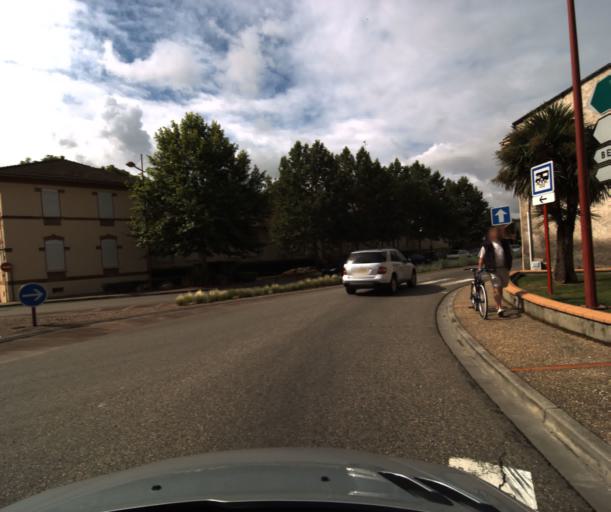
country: FR
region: Midi-Pyrenees
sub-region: Departement du Tarn-et-Garonne
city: Castelsarrasin
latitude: 44.0419
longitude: 1.1050
